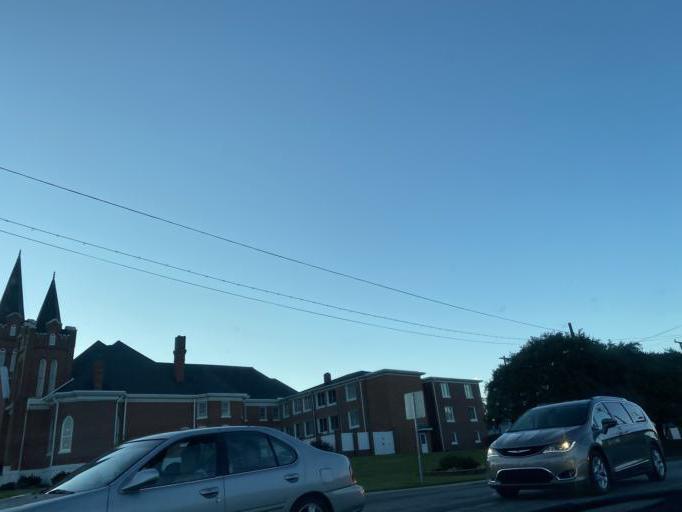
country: US
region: South Carolina
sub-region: Cherokee County
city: East Gaffney
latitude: 35.0793
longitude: -81.6375
